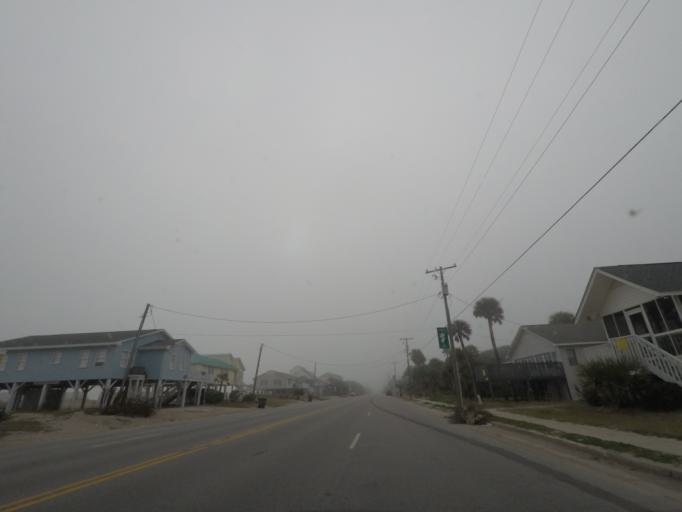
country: US
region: South Carolina
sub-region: Charleston County
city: Seabrook Island
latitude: 32.5013
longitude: -80.2997
